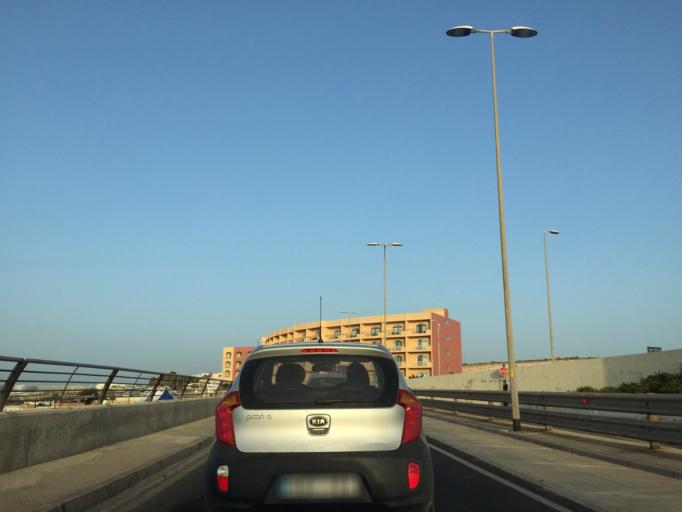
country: MT
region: Il-Mellieha
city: Mellieha
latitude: 35.9870
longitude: 14.3298
